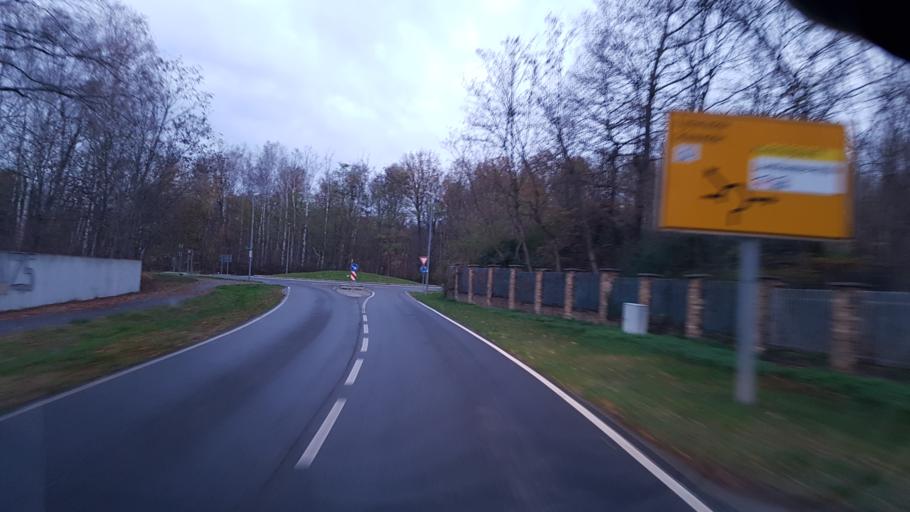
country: DE
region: Brandenburg
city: Lauchhammer
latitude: 51.4914
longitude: 13.7303
